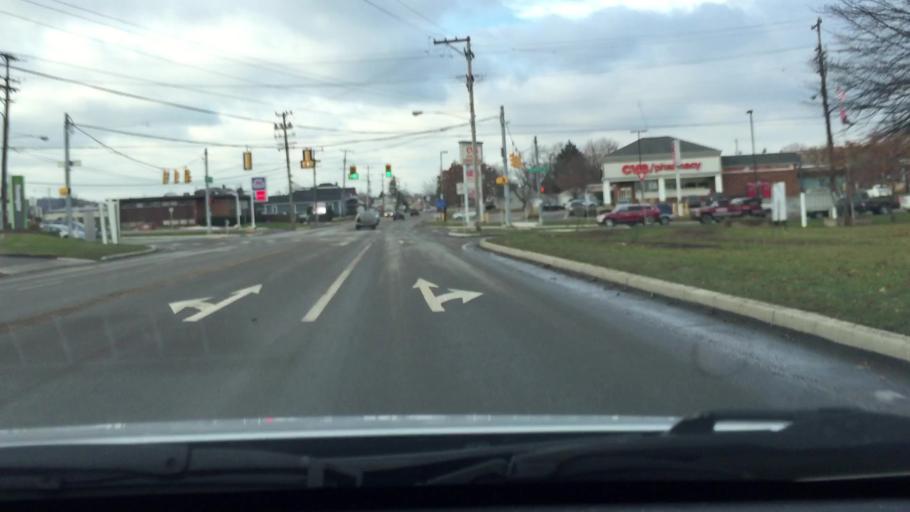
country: US
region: Pennsylvania
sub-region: Beaver County
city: Aliquippa
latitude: 40.6084
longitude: -80.2819
